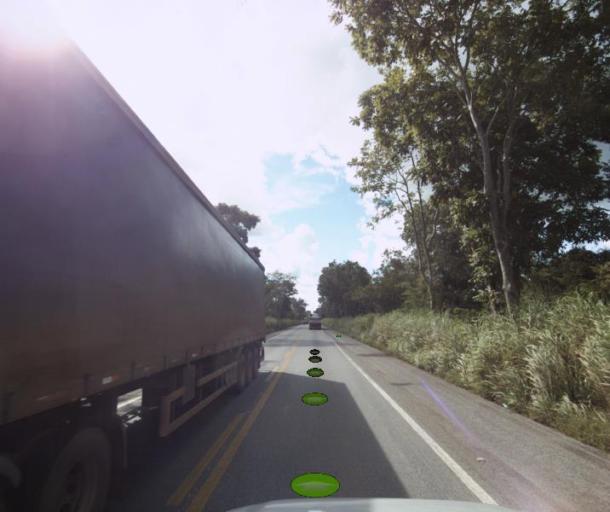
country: BR
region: Goias
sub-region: Porangatu
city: Porangatu
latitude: -13.1554
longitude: -49.1811
